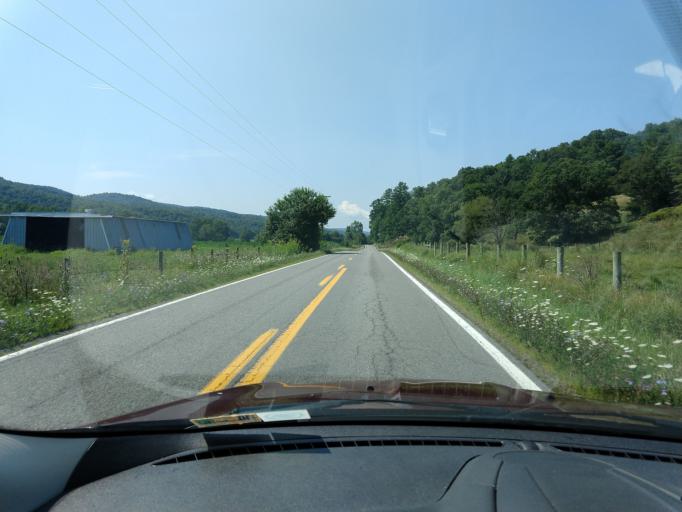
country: US
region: West Virginia
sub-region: Pocahontas County
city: Marlinton
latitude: 38.2304
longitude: -79.9097
